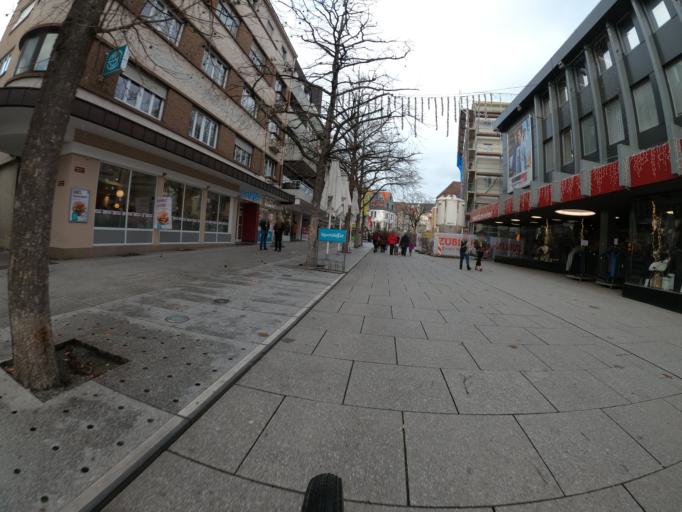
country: DE
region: Baden-Wuerttemberg
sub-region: Regierungsbezirk Stuttgart
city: Goeppingen
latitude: 48.7016
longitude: 9.6535
